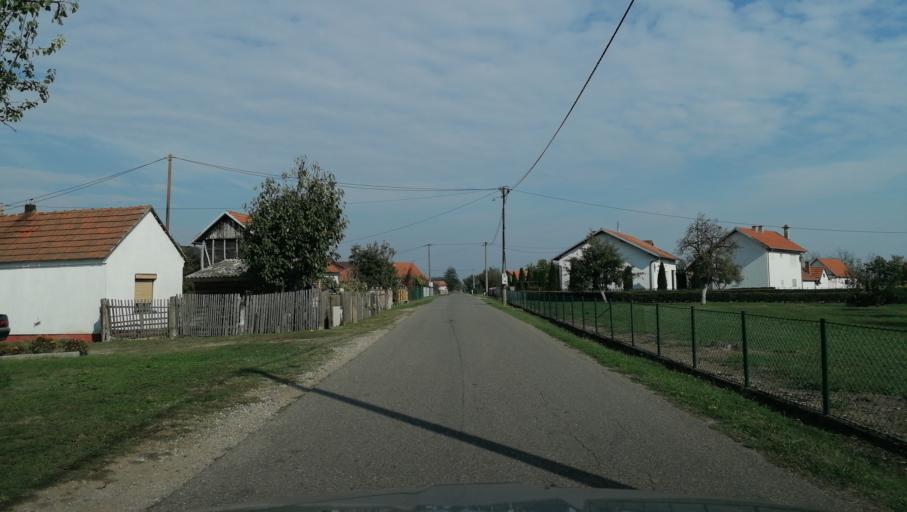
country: BA
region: Republika Srpska
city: Popovi
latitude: 44.7768
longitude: 19.2730
